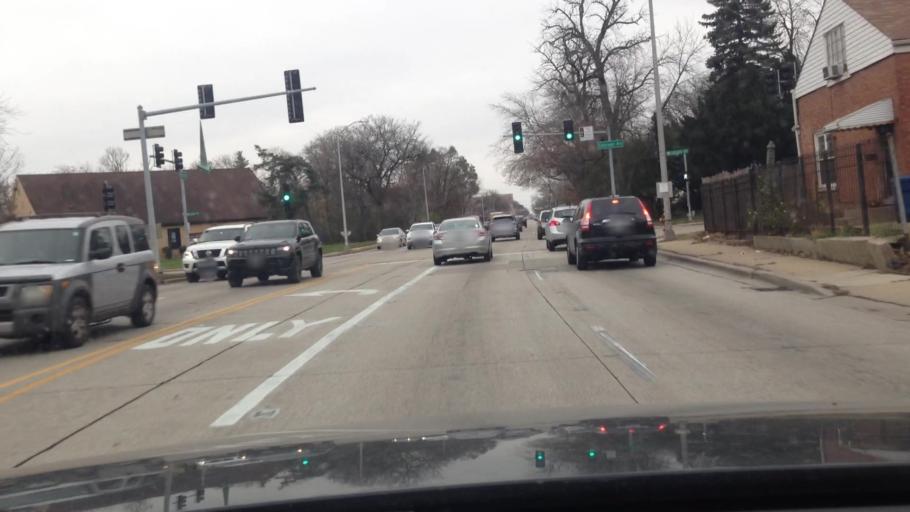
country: US
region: Illinois
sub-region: Cook County
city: Maywood
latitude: 41.8941
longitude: -87.8347
